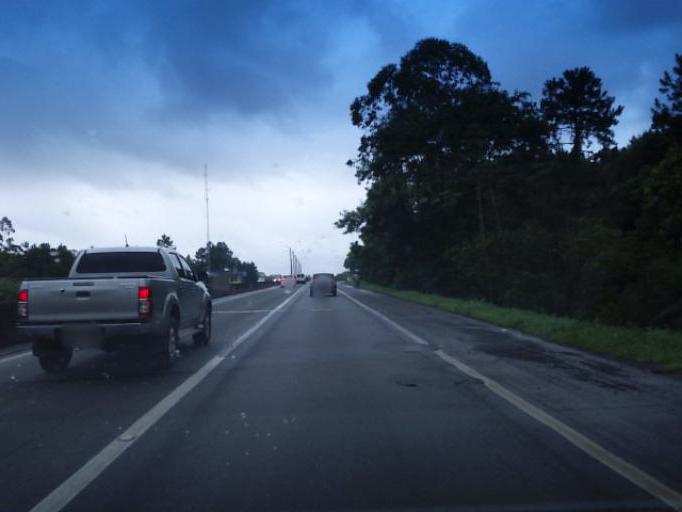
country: BR
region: Santa Catarina
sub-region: Barra Velha
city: Barra Velha
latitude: -26.6121
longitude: -48.7213
